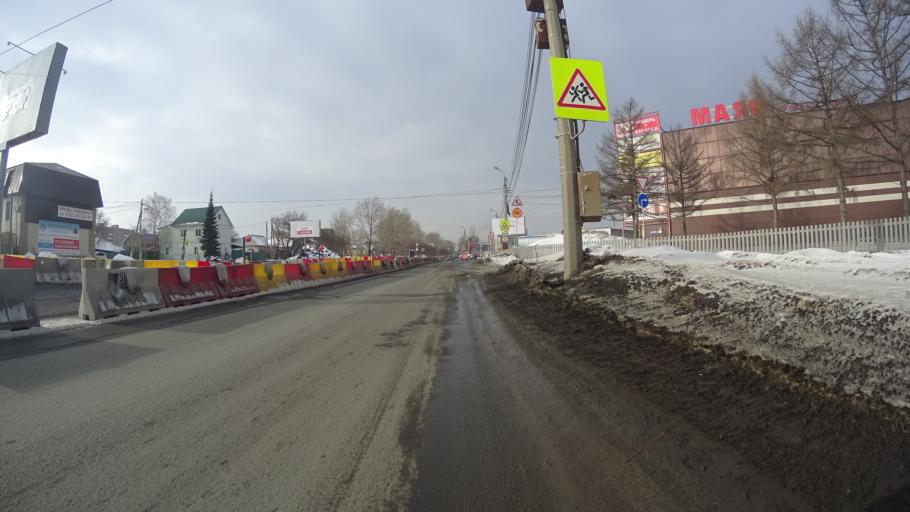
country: RU
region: Chelyabinsk
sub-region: Gorod Chelyabinsk
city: Chelyabinsk
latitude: 55.1181
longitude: 61.3852
